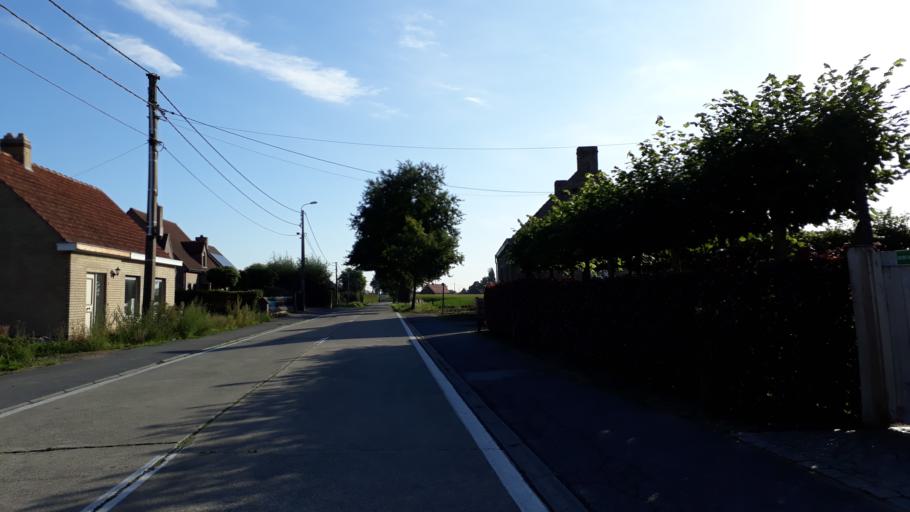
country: BE
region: Flanders
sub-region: Provincie West-Vlaanderen
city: Torhout
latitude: 51.0825
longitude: 3.1447
